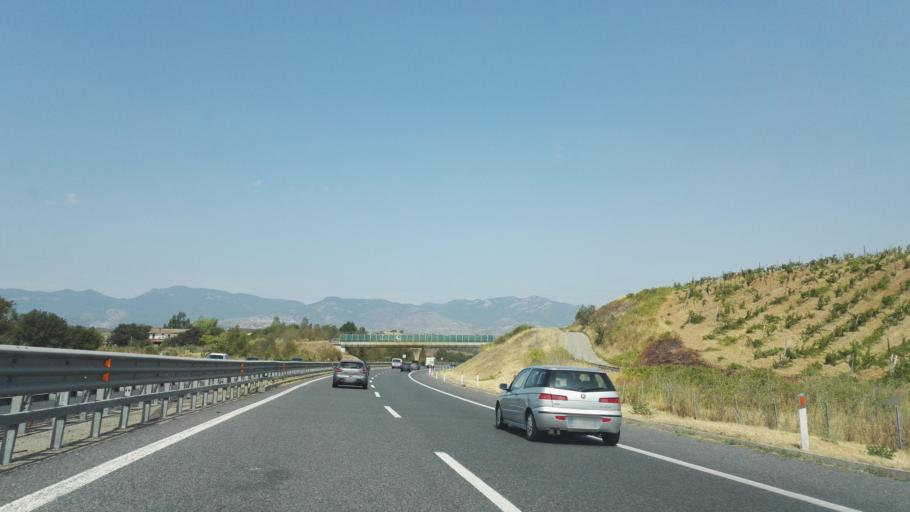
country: IT
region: Calabria
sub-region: Provincia di Cosenza
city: Tarsia
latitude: 39.6476
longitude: 16.2197
